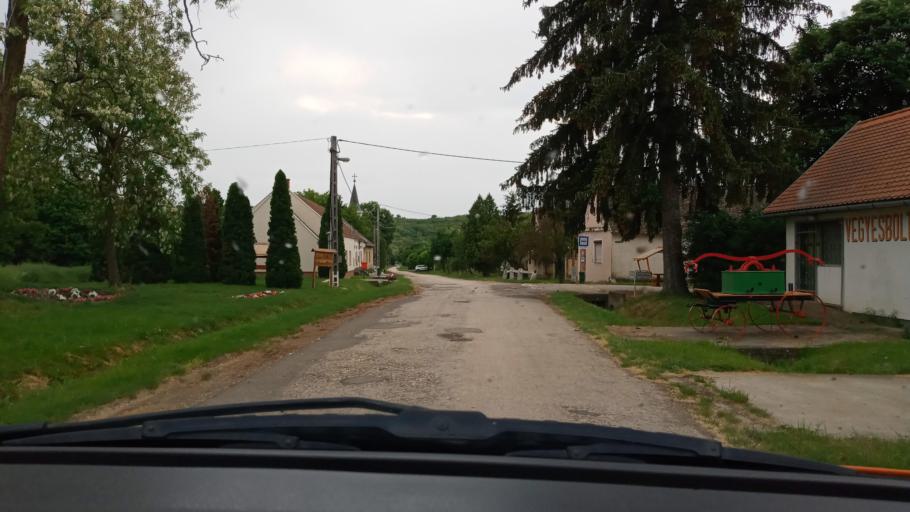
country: HU
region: Baranya
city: Harkany
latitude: 45.9005
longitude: 18.1369
